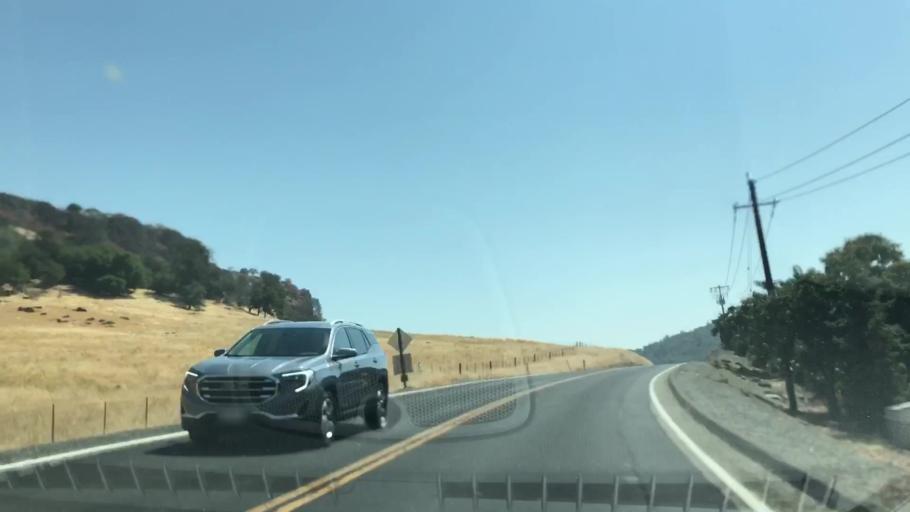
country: US
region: California
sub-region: Calaveras County
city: Copperopolis
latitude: 37.9032
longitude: -120.5812
